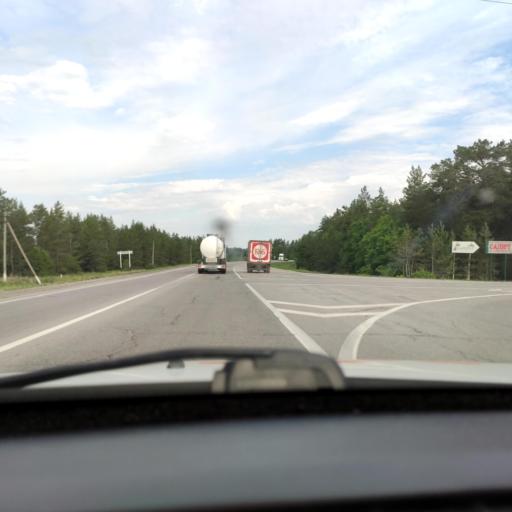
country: RU
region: Samara
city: Mirnyy
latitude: 53.5286
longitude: 50.3085
